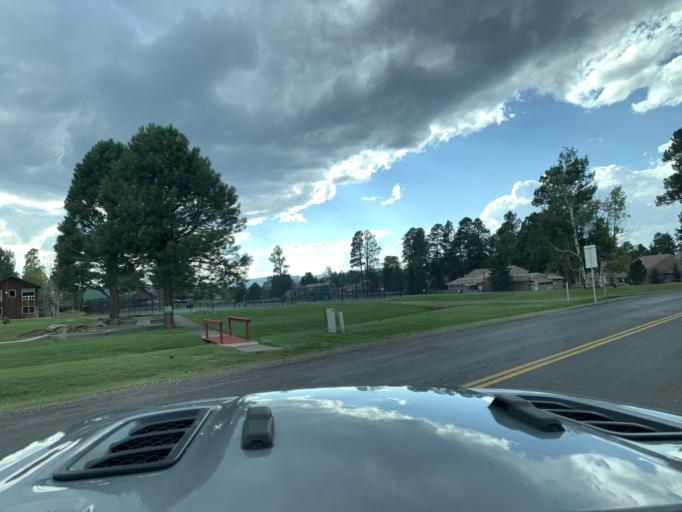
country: US
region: Colorado
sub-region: Archuleta County
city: Pagosa Springs
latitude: 37.2596
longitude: -107.0706
